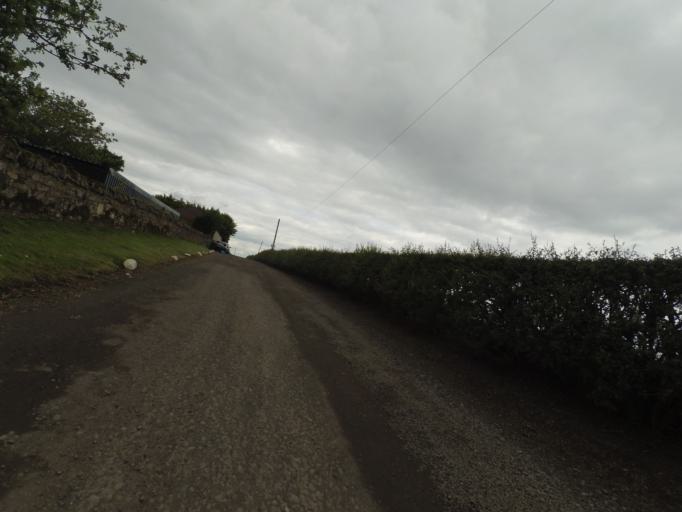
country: GB
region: Scotland
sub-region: East Lothian
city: Prestonpans
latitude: 55.9164
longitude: -2.9972
